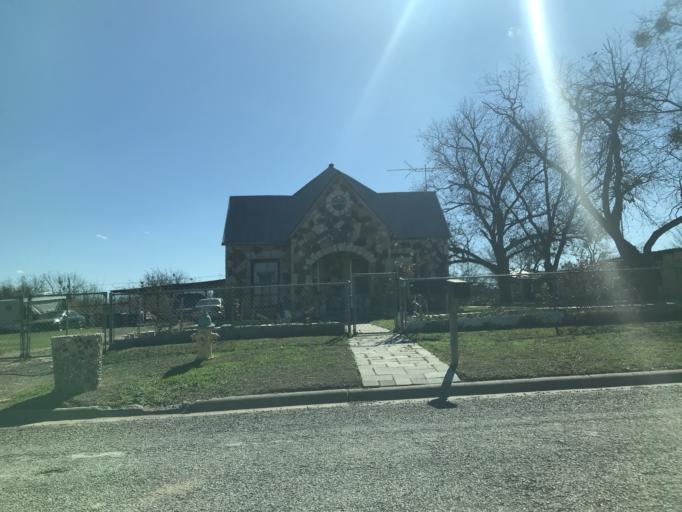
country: US
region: Texas
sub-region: Tom Green County
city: San Angelo
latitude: 31.4643
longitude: -100.4111
